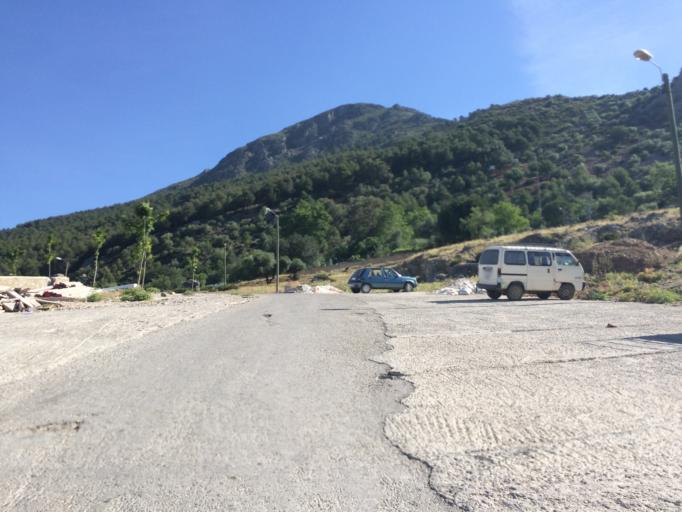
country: MA
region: Tanger-Tetouan
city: Chefchaouene
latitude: 35.1716
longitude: -5.2612
